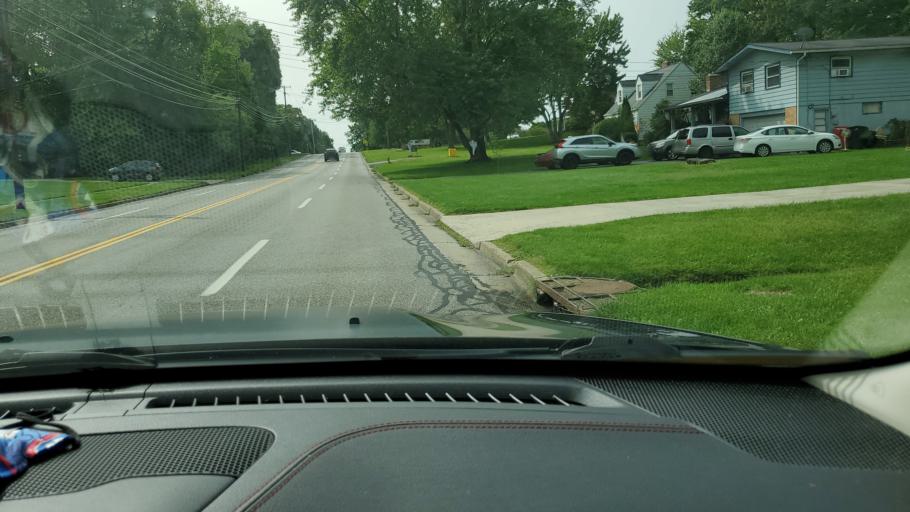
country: US
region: Ohio
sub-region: Mahoning County
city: Boardman
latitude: 41.0174
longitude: -80.6724
